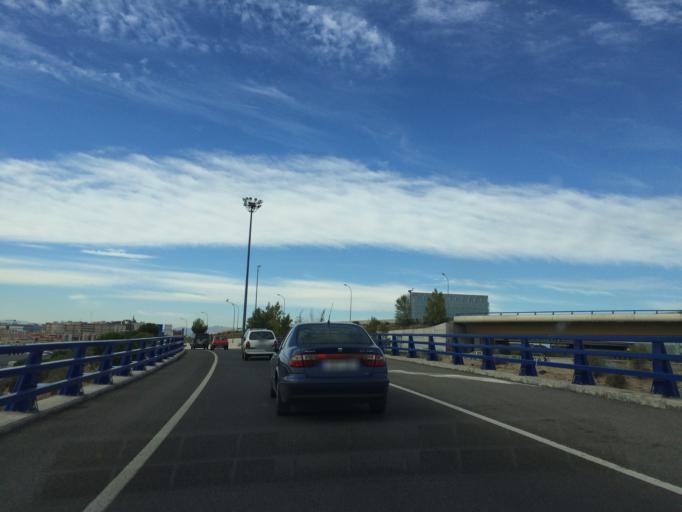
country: ES
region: Madrid
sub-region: Provincia de Madrid
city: Las Tablas
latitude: 40.5094
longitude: -3.6589
